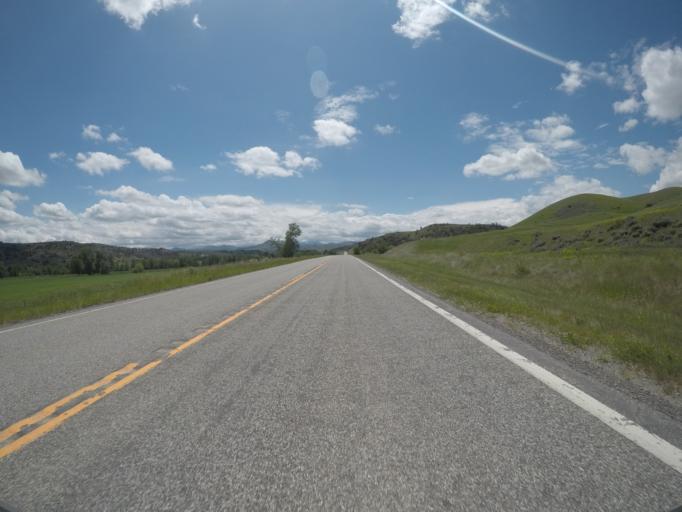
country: US
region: Montana
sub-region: Sweet Grass County
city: Big Timber
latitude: 45.7474
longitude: -109.9946
